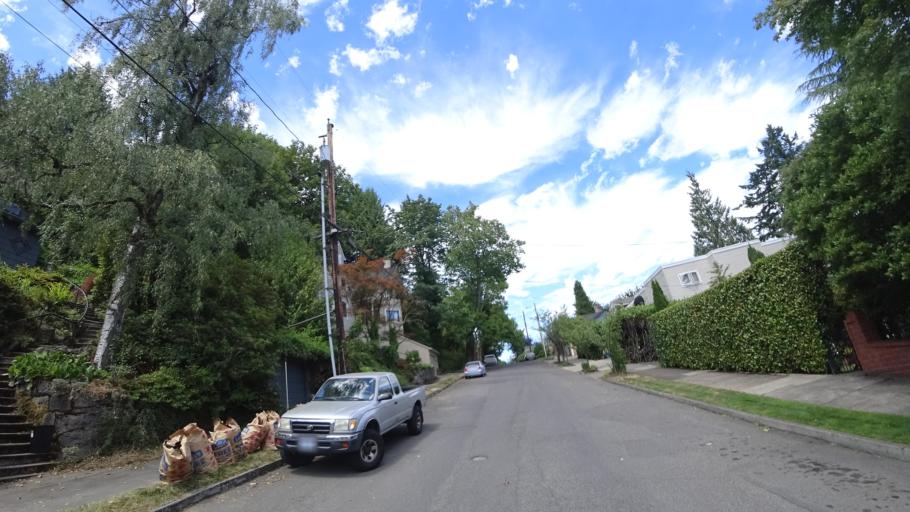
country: US
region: Oregon
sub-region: Multnomah County
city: Portland
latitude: 45.5082
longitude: -122.6979
